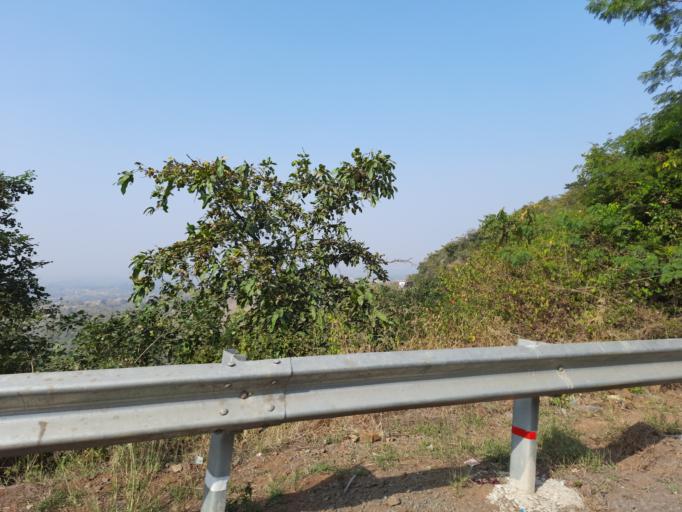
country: IN
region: Maharashtra
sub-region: Nashik Division
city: Surgana
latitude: 20.2583
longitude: 73.6187
